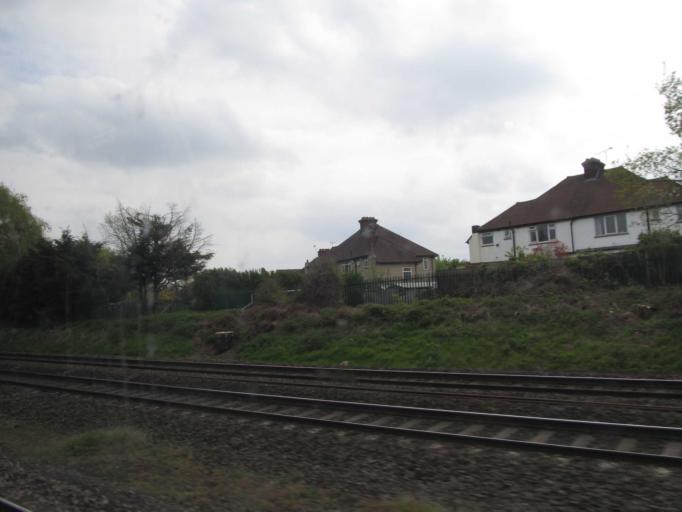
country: GB
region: England
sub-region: Buckinghamshire
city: Iver
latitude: 51.5082
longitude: -0.5128
